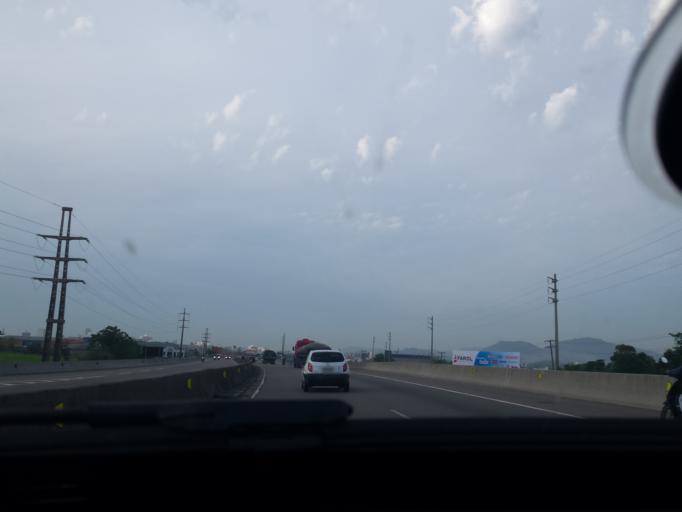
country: BR
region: Santa Catarina
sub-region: Tubarao
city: Tubarao
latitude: -28.4608
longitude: -48.9903
